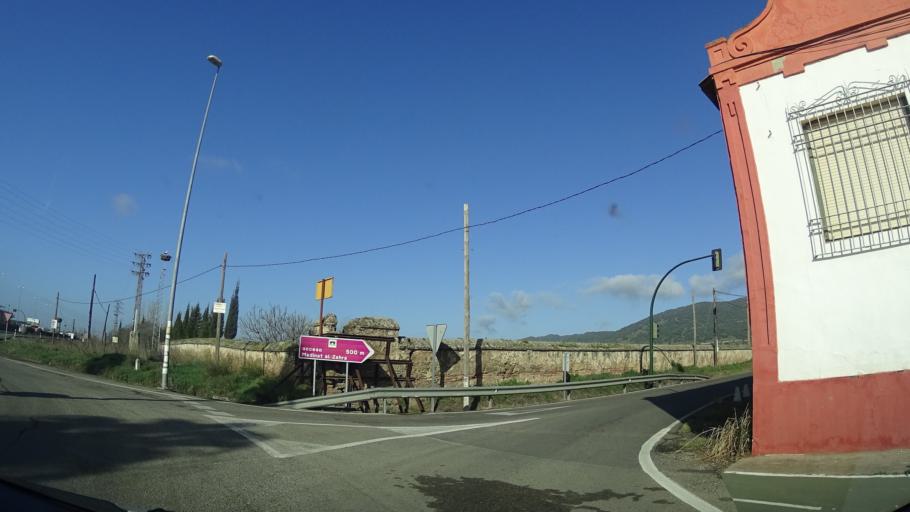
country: ES
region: Andalusia
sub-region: Province of Cordoba
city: Villarrubia
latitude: 37.8758
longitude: -4.8488
